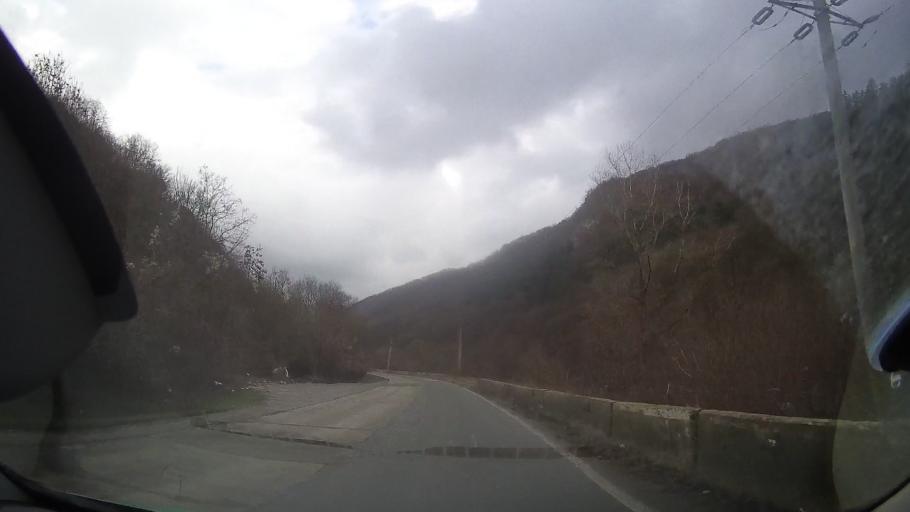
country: RO
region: Cluj
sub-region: Comuna Moldovenesti
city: Moldovenesti
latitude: 46.5024
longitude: 23.6235
